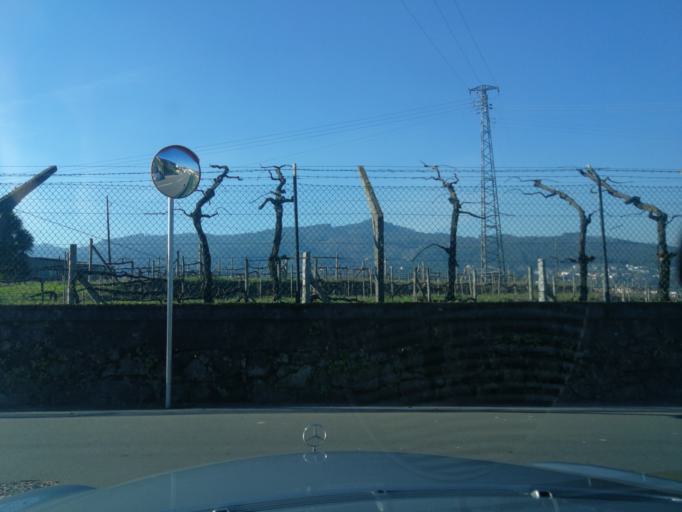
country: PT
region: Braga
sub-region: Guimaraes
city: Ponte
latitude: 41.4918
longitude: -8.3521
